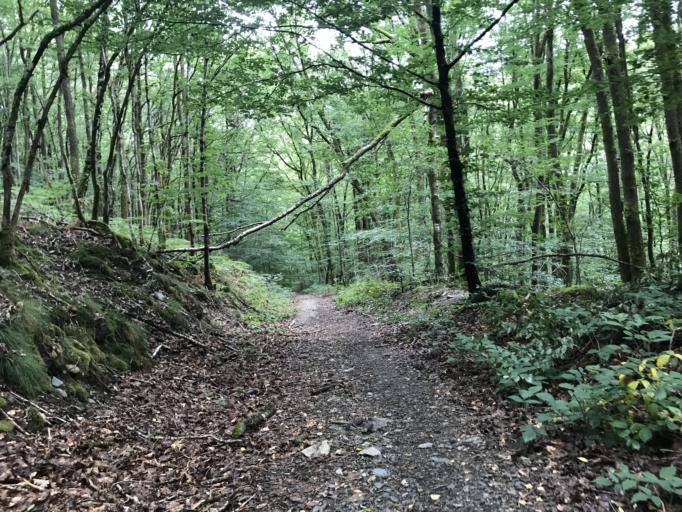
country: FR
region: Champagne-Ardenne
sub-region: Departement des Ardennes
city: Montherme
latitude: 49.8921
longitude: 4.7610
